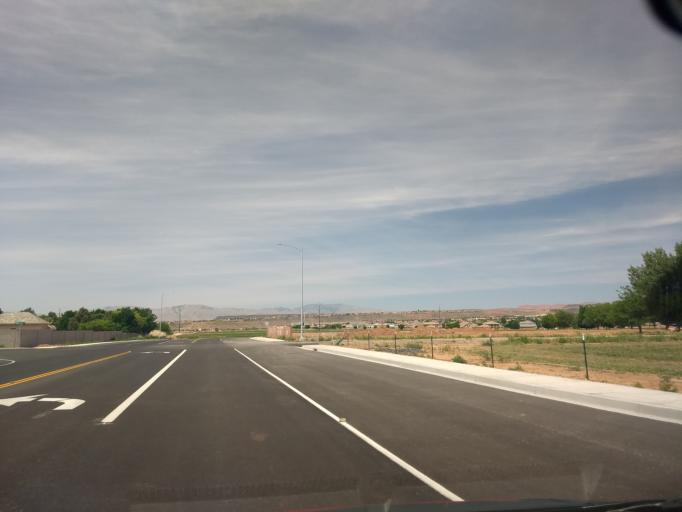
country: US
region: Utah
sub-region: Washington County
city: Washington
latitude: 37.0944
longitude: -113.5038
